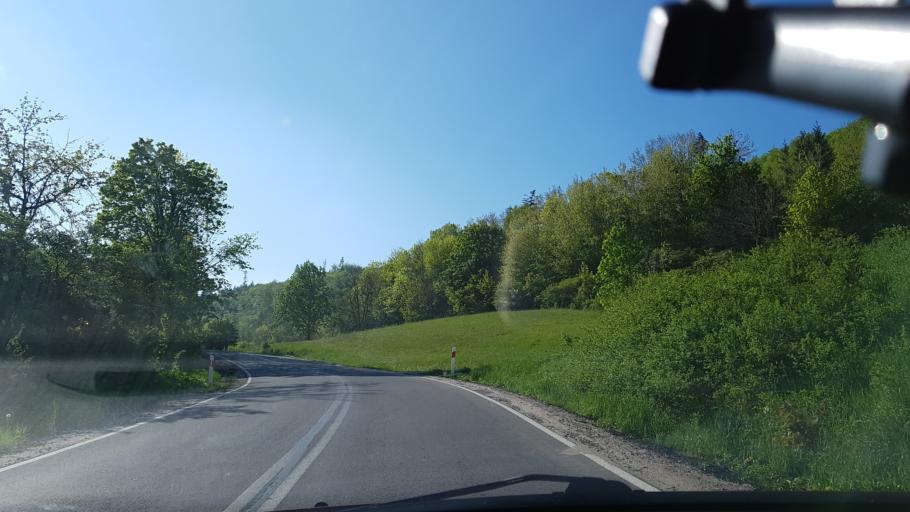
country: PL
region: Lower Silesian Voivodeship
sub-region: Powiat klodzki
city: Bozkow
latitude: 50.5702
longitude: 16.6247
